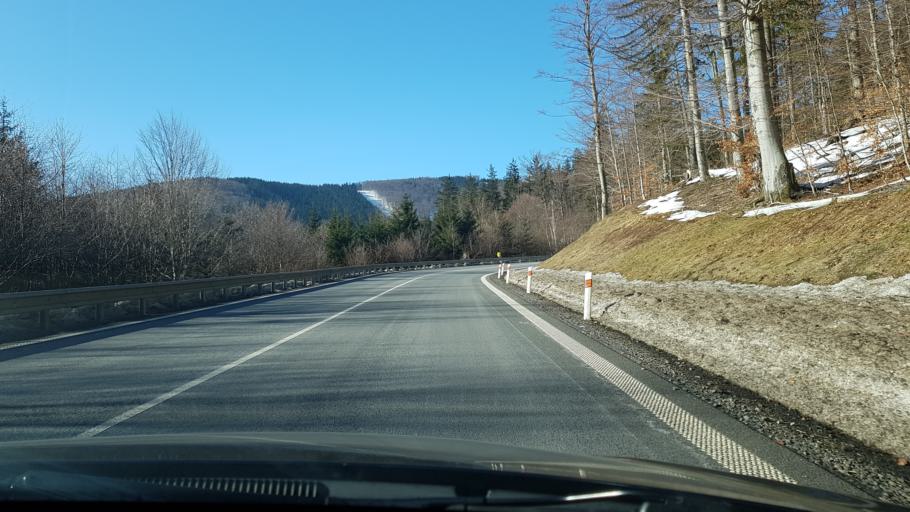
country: CZ
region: Olomoucky
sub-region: Okres Sumperk
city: Loucna nad Desnou
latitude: 50.1074
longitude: 17.1453
